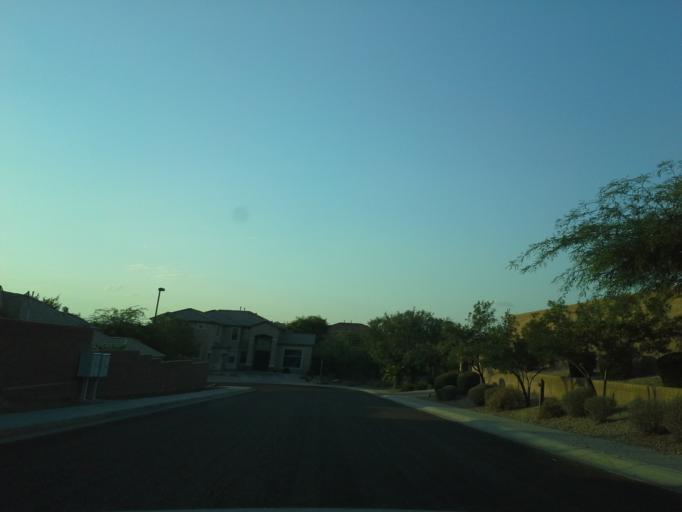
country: US
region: Arizona
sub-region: Maricopa County
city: Anthem
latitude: 33.7521
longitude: -112.1015
